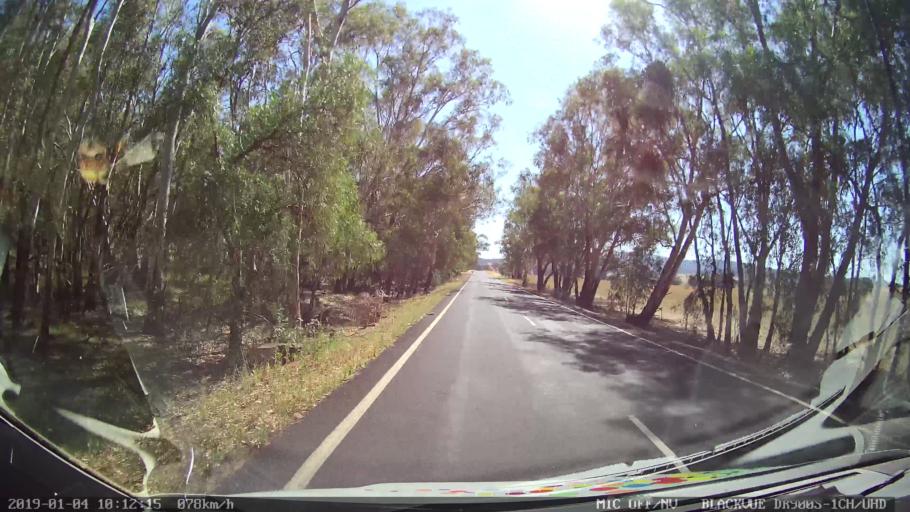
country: AU
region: New South Wales
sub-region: Cabonne
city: Canowindra
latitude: -33.4135
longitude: 148.3924
